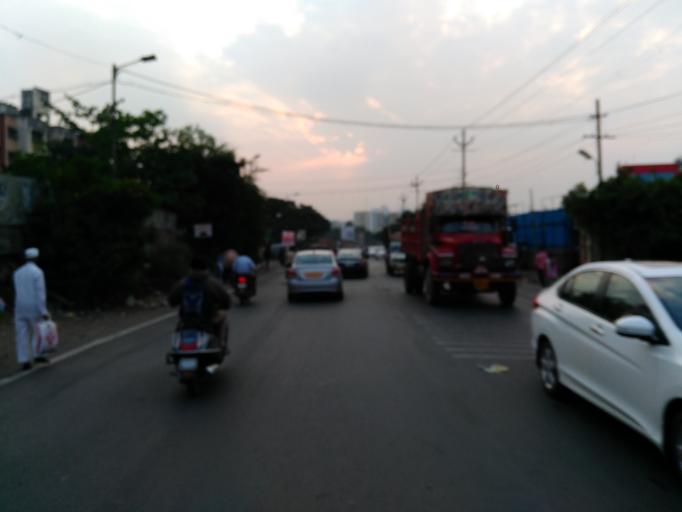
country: IN
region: Maharashtra
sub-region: Pune Division
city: Pune
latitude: 18.4492
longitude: 73.8705
